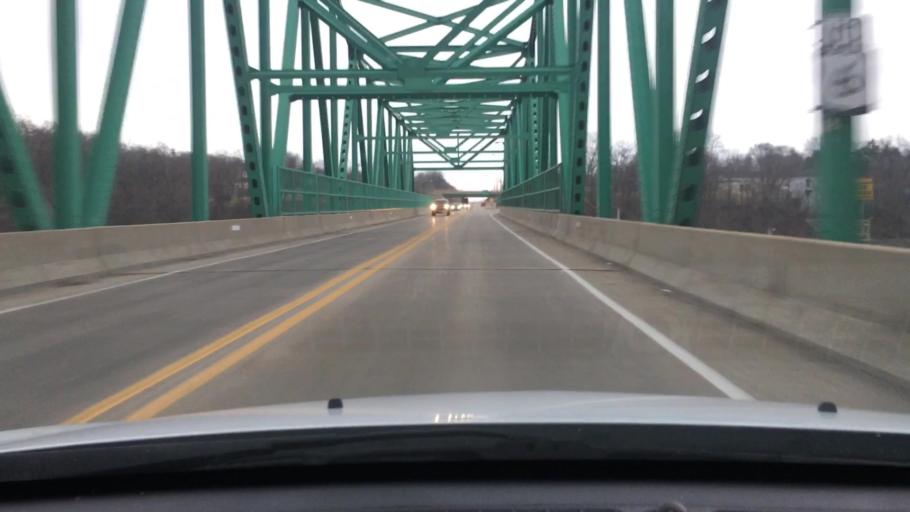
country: US
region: Illinois
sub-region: LaSalle County
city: Peru
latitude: 41.3243
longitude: -89.1199
